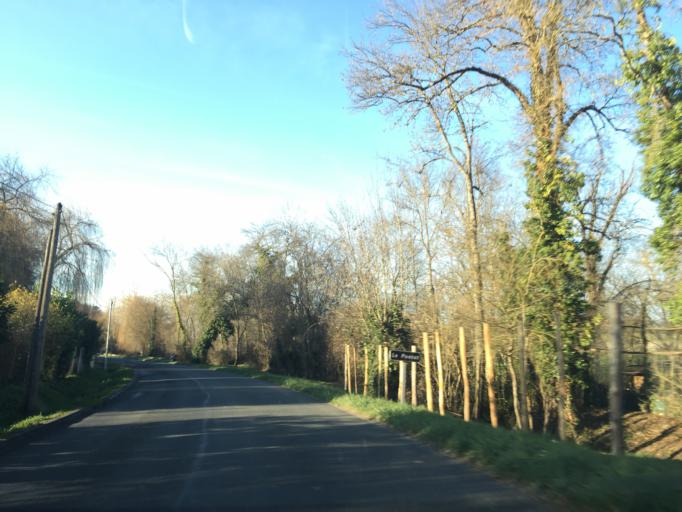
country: FR
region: Aquitaine
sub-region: Departement de la Dordogne
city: Saint-Aulaye
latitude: 45.2488
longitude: 0.2169
